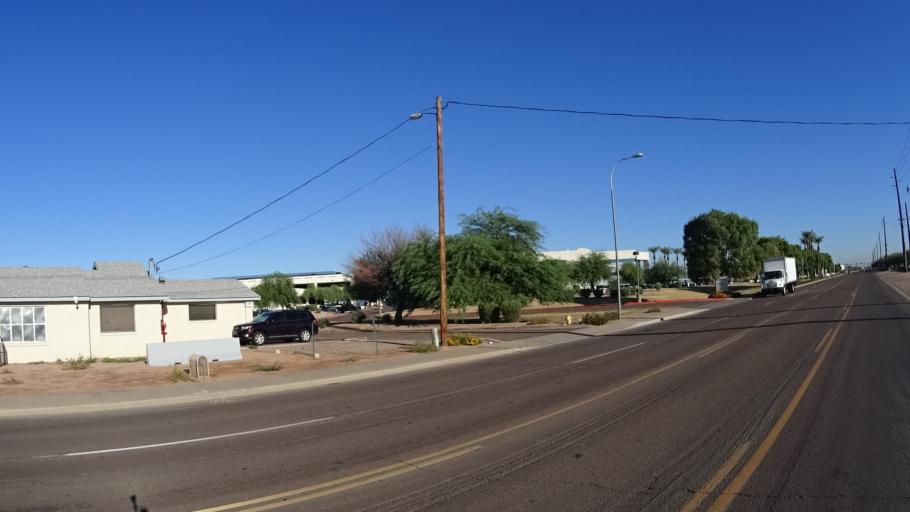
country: US
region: Arizona
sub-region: Maricopa County
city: Tolleson
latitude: 33.4256
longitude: -112.2211
